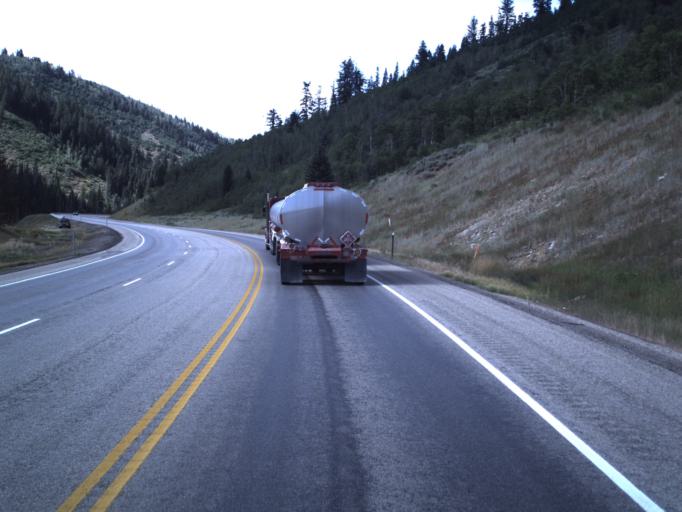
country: US
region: Utah
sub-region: Wasatch County
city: Heber
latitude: 40.3206
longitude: -111.2589
